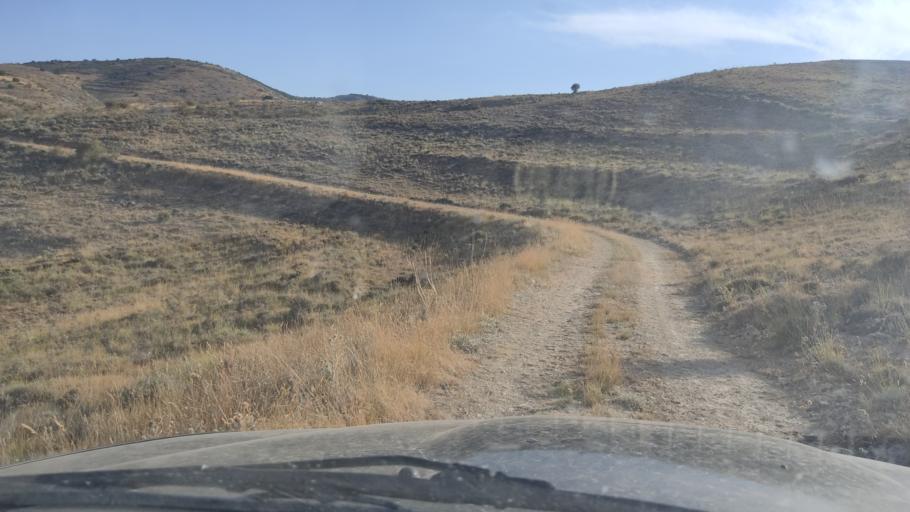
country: ES
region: Aragon
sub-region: Provincia de Teruel
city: Monforte de Moyuela
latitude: 41.0330
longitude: -1.0230
